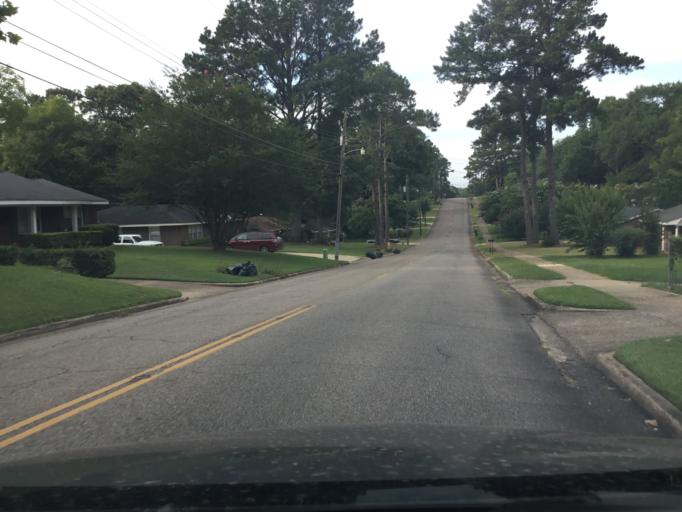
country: US
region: Alabama
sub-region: Montgomery County
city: Montgomery
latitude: 32.3736
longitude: -86.2555
